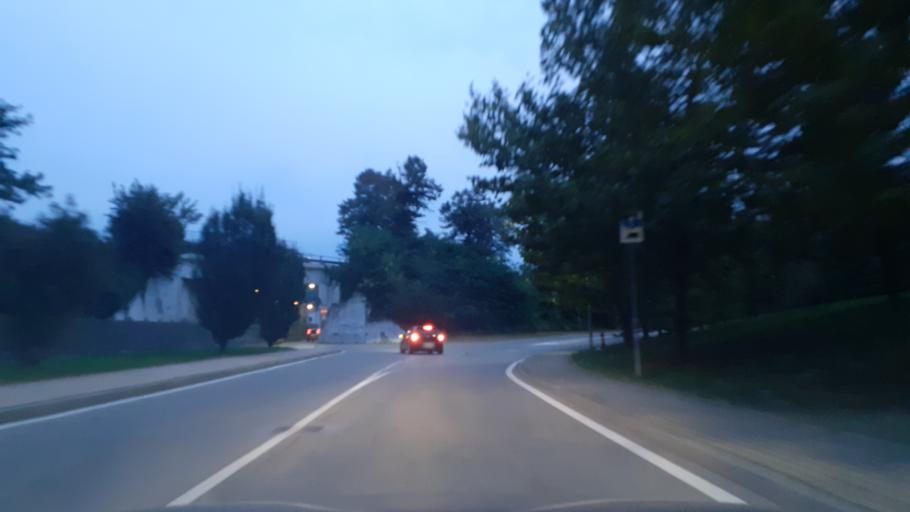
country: IT
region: Lombardy
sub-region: Provincia di Lecco
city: Bulciago
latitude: 45.7482
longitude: 9.2816
